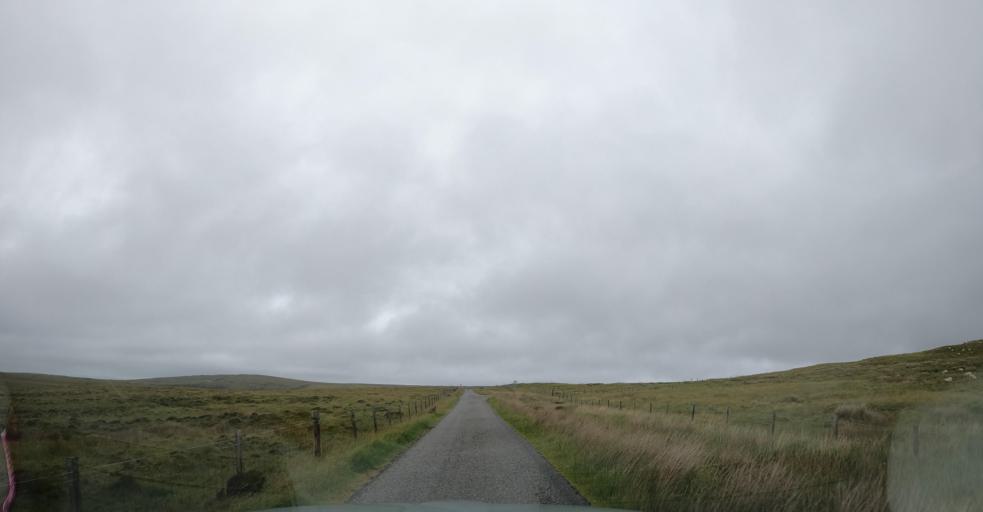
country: GB
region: Scotland
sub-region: Eilean Siar
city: Isle of North Uist
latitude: 57.5958
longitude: -7.3863
